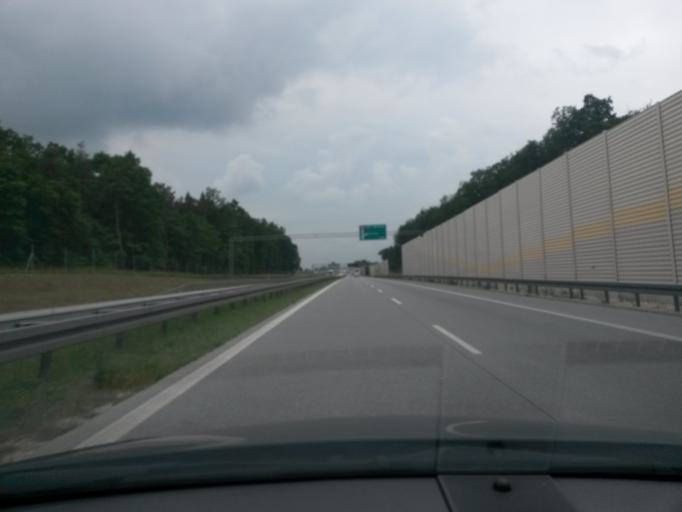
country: PL
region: Lodz Voivodeship
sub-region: Powiat rawski
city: Rawa Mazowiecka
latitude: 51.8111
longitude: 20.3087
